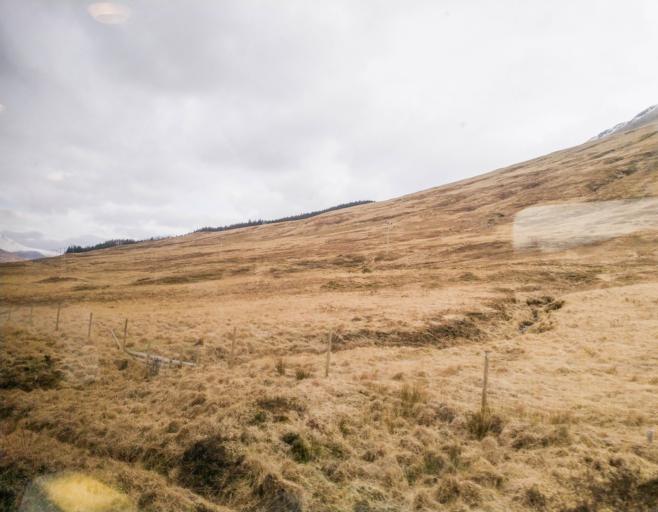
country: GB
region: Scotland
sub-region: Argyll and Bute
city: Garelochhead
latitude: 56.4995
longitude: -4.7498
